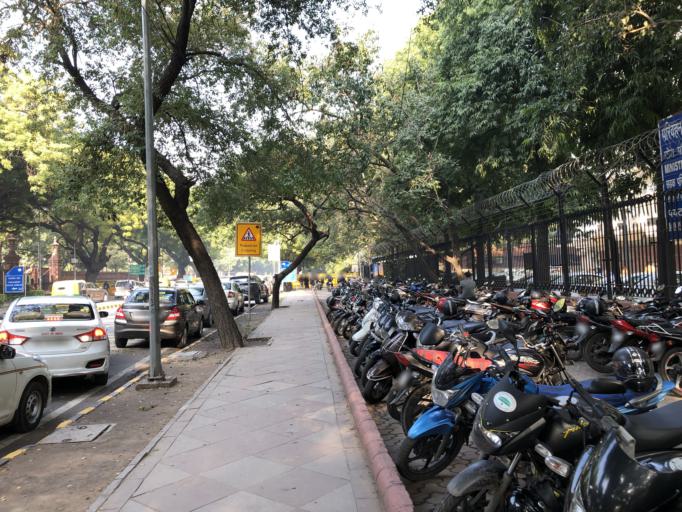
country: IN
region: NCT
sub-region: New Delhi
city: New Delhi
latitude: 28.6192
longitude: 77.2099
